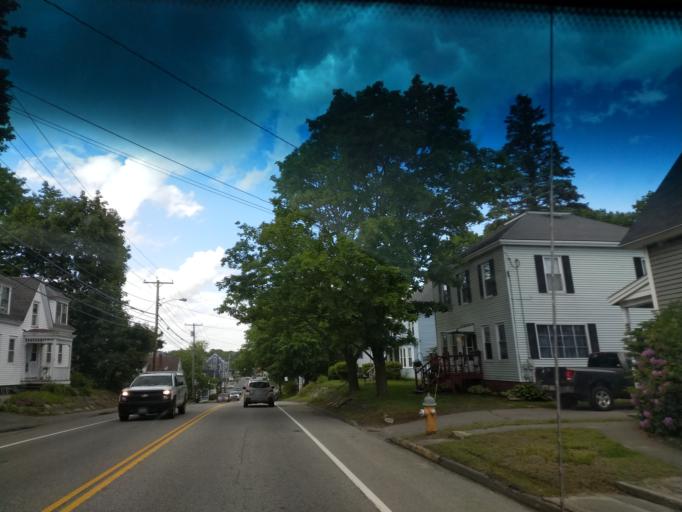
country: US
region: Maine
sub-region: Cumberland County
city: Westbrook
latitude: 43.6737
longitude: -70.3621
